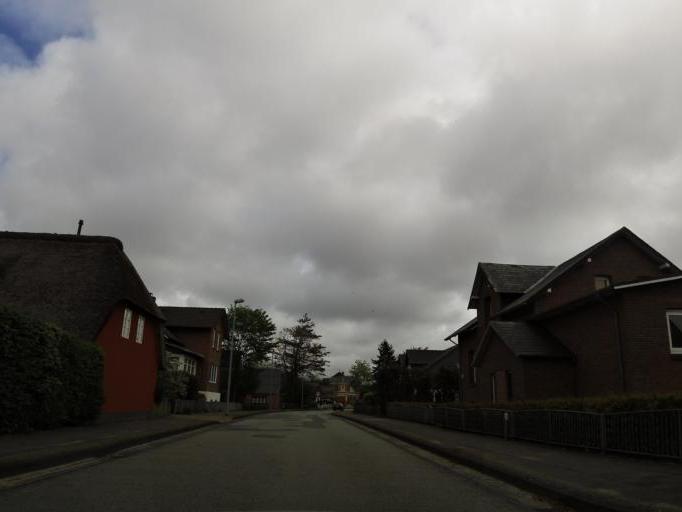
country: DE
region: Schleswig-Holstein
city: Niebull
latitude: 54.7802
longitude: 8.8201
